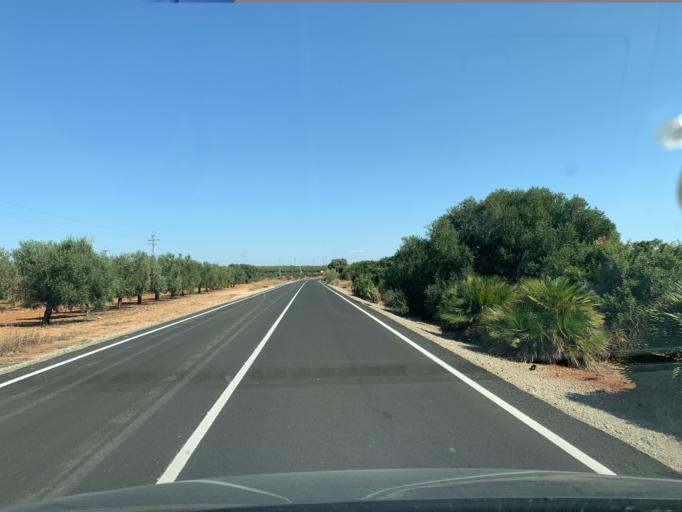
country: ES
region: Andalusia
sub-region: Provincia de Sevilla
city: La Lantejuela
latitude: 37.3342
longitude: -5.3004
